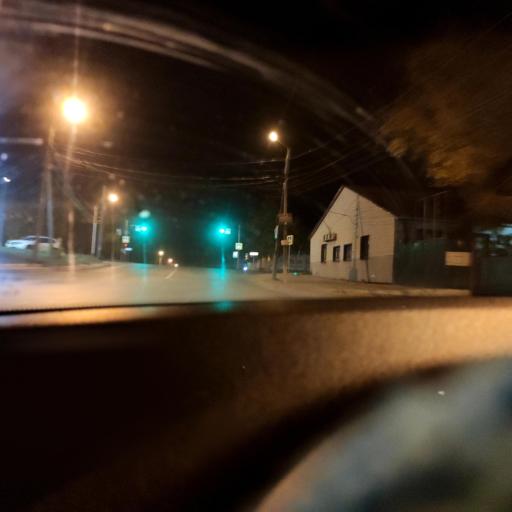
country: RU
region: Samara
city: Samara
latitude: 53.1835
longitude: 50.1626
